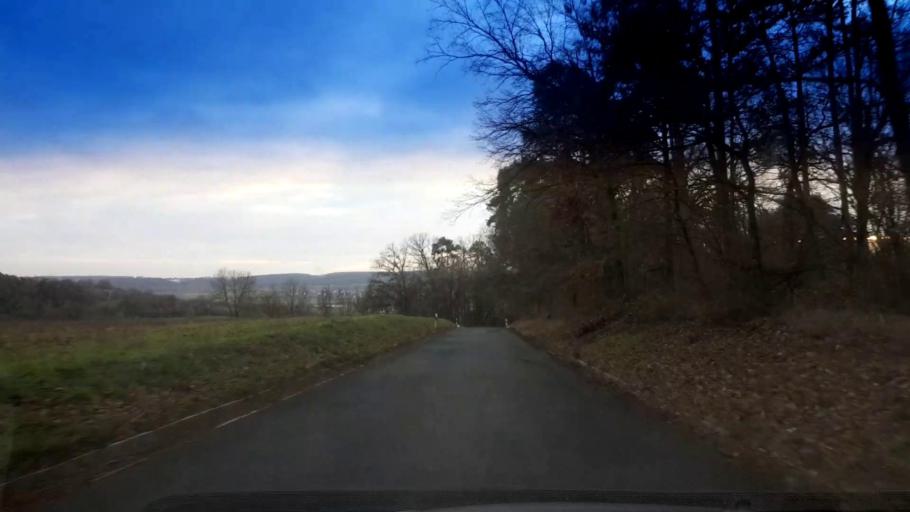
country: DE
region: Bavaria
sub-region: Upper Franconia
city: Lauter
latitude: 49.9563
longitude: 10.7608
